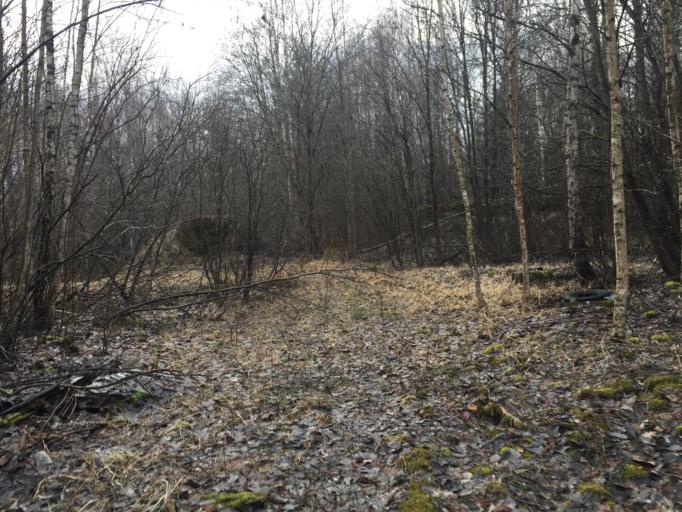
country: LV
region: Daugavpils
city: Daugavpils
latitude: 55.9496
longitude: 26.6617
